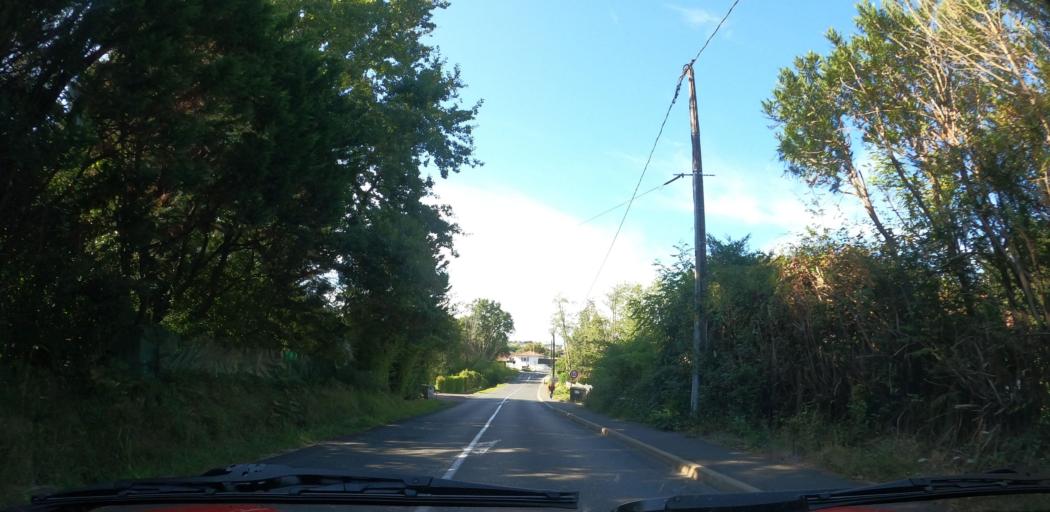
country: FR
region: Aquitaine
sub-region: Departement des Pyrenees-Atlantiques
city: Arbonne
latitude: 43.4409
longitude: -1.5467
